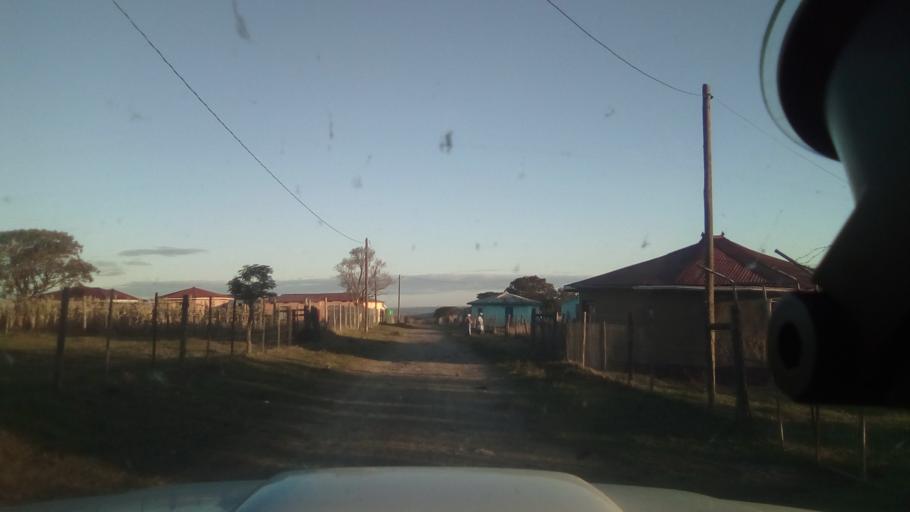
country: ZA
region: Eastern Cape
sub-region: Buffalo City Metropolitan Municipality
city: Bhisho
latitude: -32.7395
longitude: 27.3764
